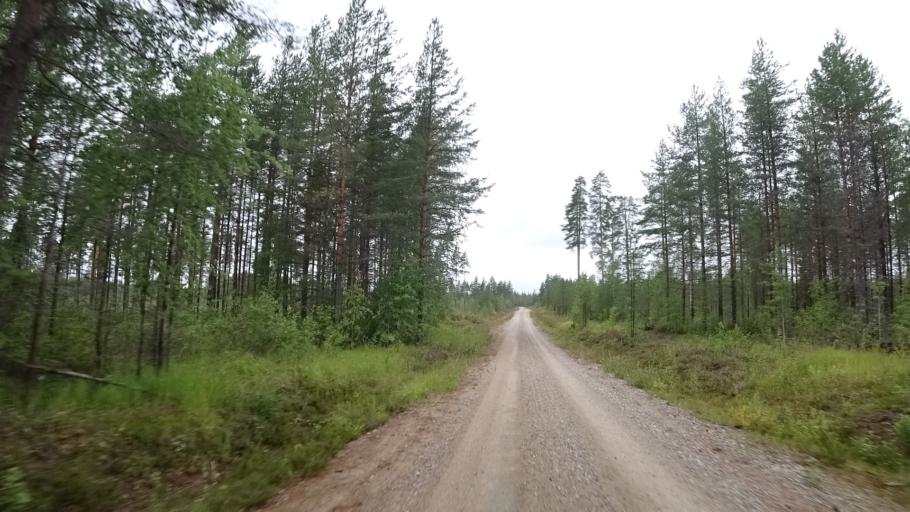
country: FI
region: North Karelia
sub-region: Pielisen Karjala
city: Lieksa
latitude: 63.5124
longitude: 30.1359
